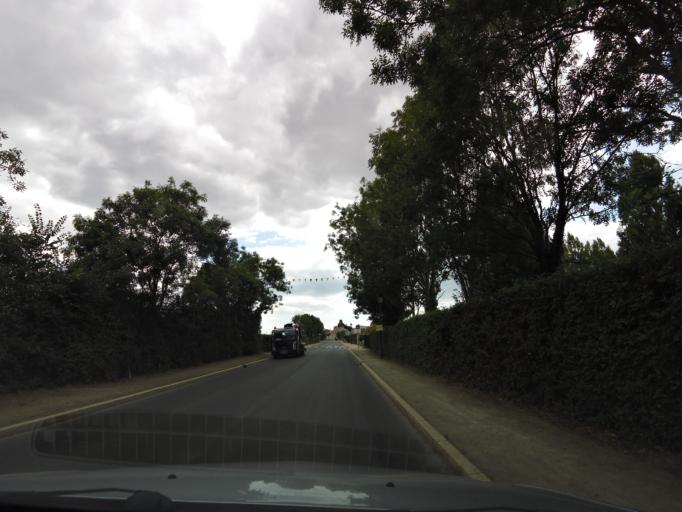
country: FR
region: Pays de la Loire
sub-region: Departement de la Vendee
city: Avrille
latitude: 46.4415
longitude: -1.4667
